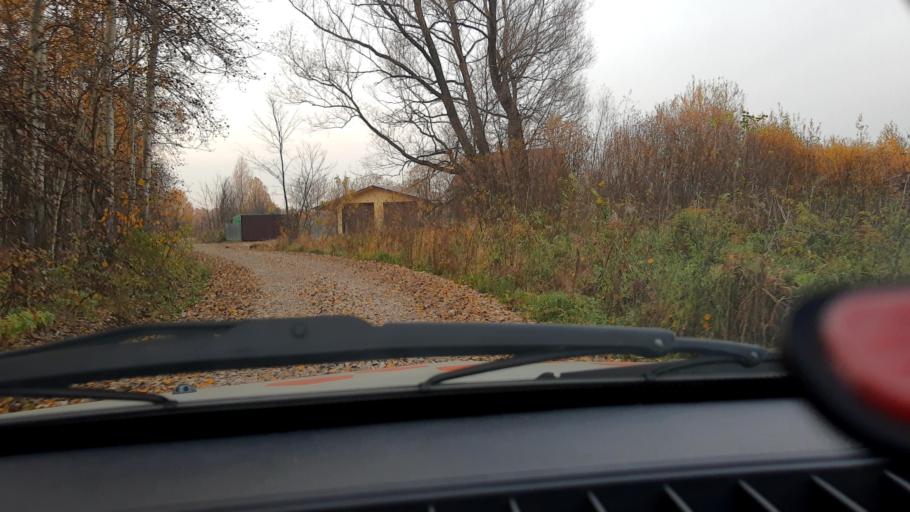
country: RU
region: Bashkortostan
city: Iglino
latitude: 54.7973
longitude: 56.3450
